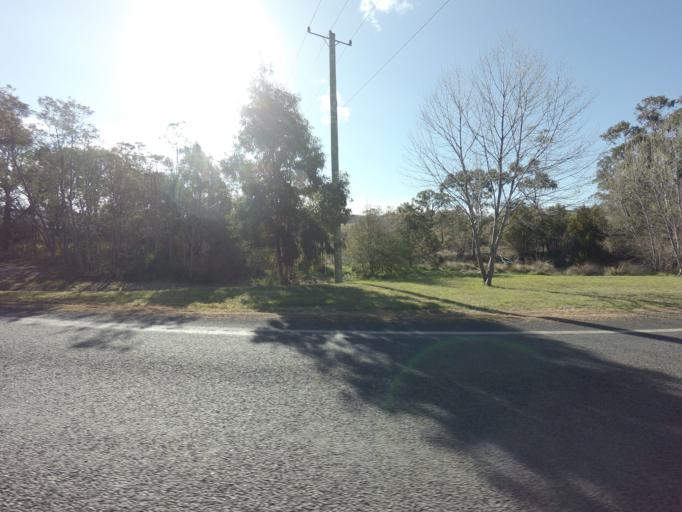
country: AU
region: Tasmania
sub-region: Sorell
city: Sorell
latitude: -42.4998
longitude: 147.9204
